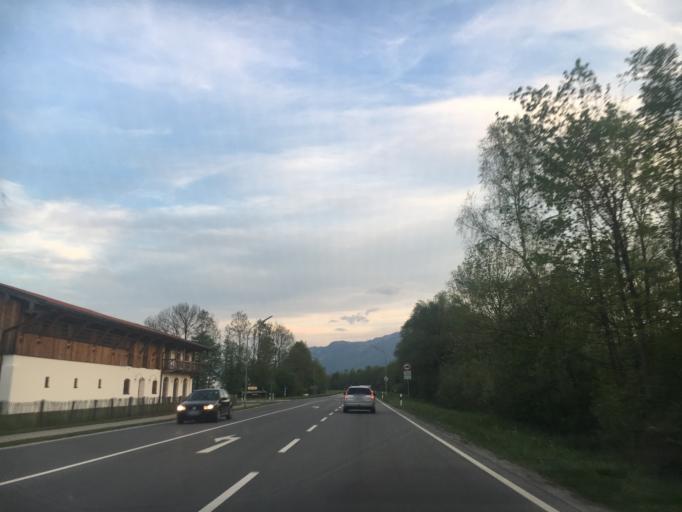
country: DE
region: Bavaria
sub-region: Upper Bavaria
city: Gaissach
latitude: 47.7424
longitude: 11.5668
